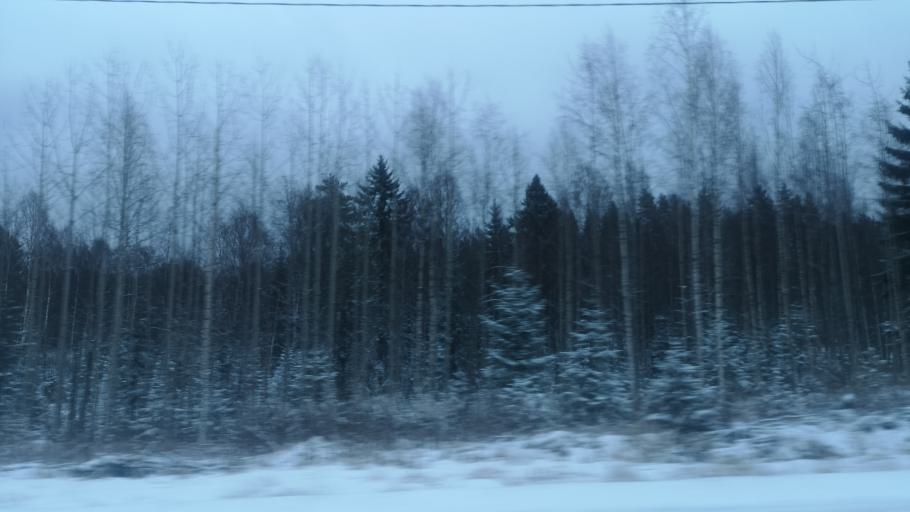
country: FI
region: Southern Savonia
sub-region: Savonlinna
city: Enonkoski
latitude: 62.0530
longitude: 28.7039
